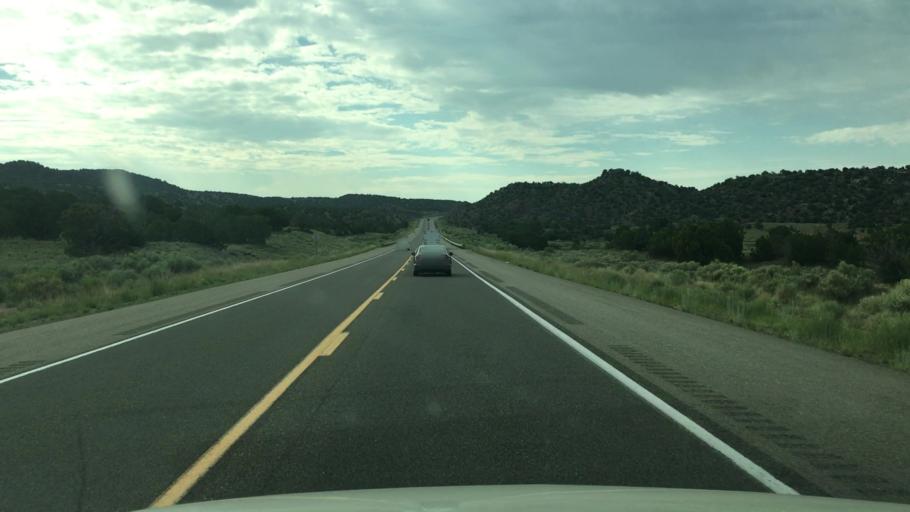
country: US
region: New Mexico
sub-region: Santa Fe County
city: Eldorado at Santa Fe
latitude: 35.2794
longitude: -105.8200
